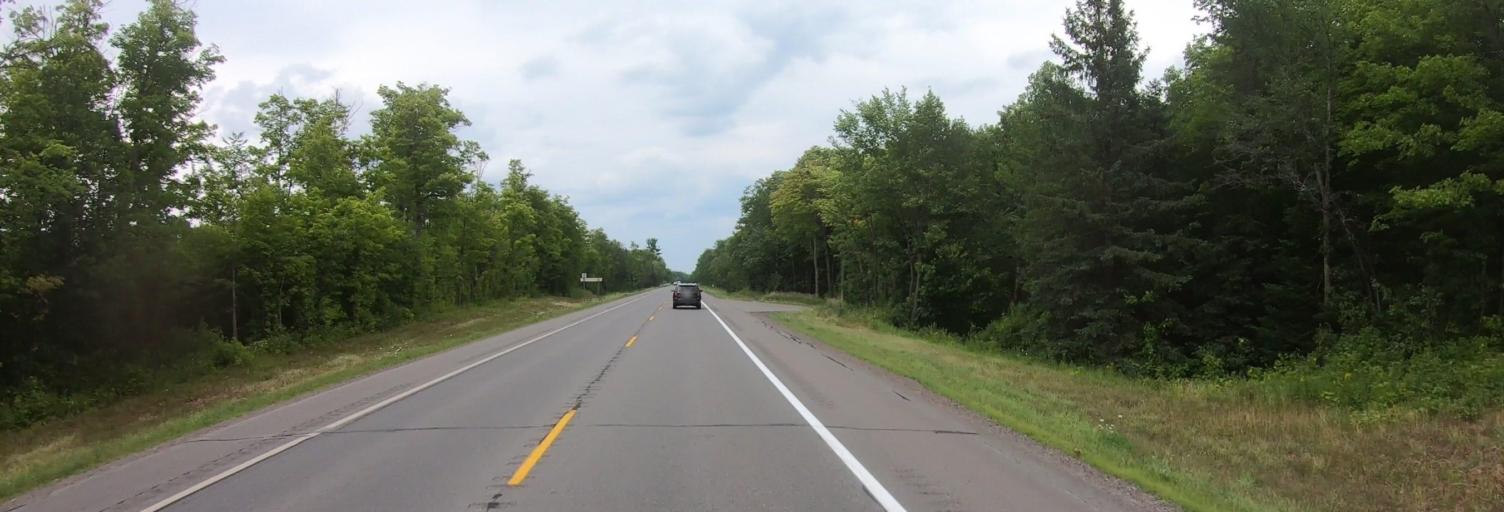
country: US
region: Michigan
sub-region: Baraga County
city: L'Anse
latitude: 46.6517
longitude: -88.4765
